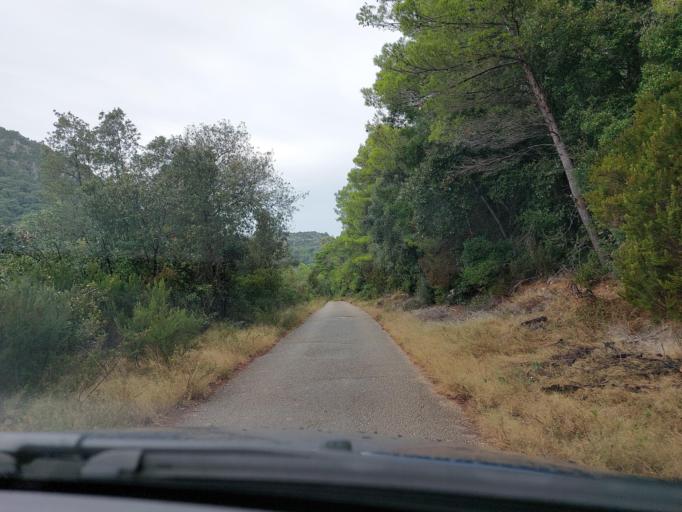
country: HR
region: Dubrovacko-Neretvanska
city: Smokvica
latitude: 42.7553
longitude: 16.9077
